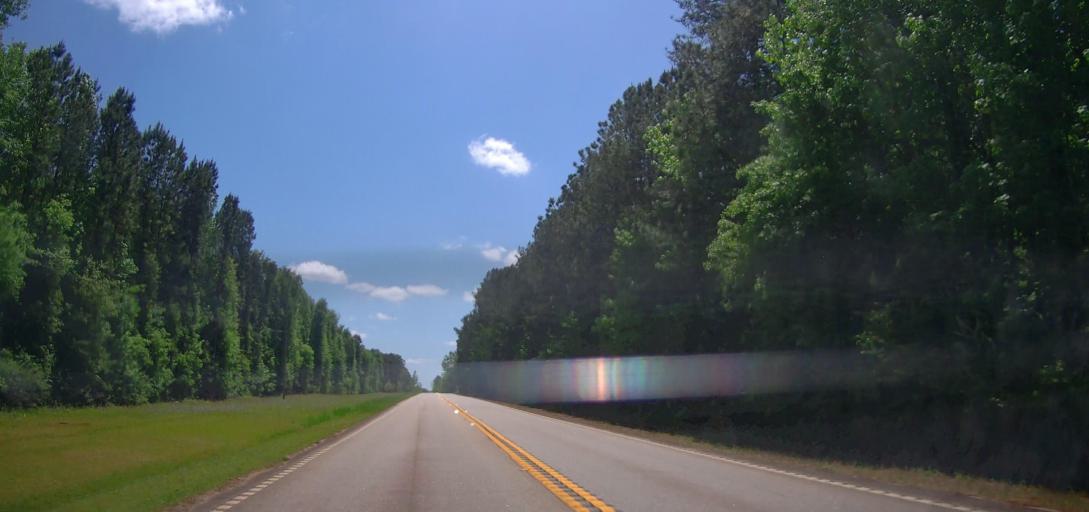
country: US
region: Georgia
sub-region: Jasper County
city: Monticello
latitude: 33.2190
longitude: -83.6686
